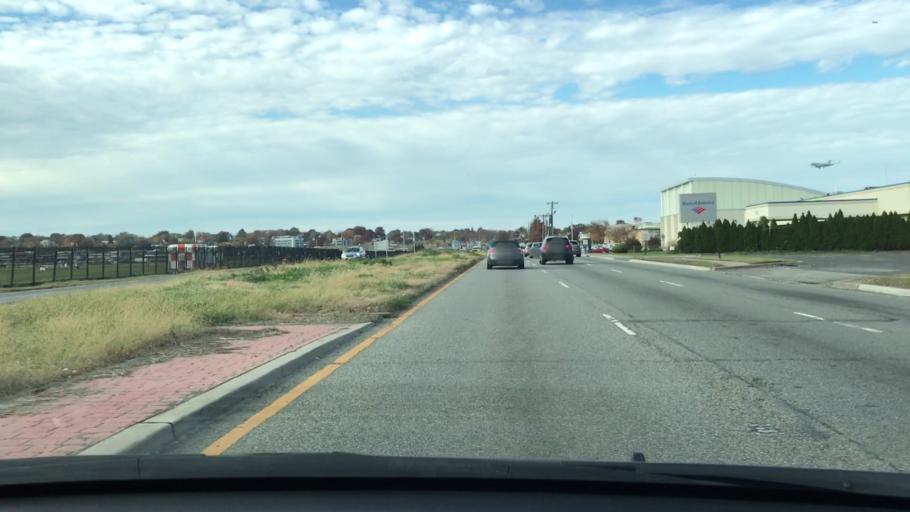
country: US
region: New Jersey
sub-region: Bergen County
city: Little Ferry
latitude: 40.8585
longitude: -74.0530
